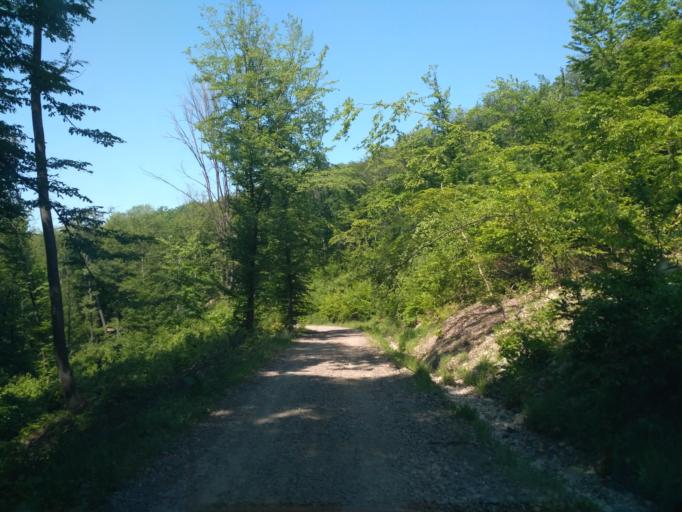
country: SK
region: Presovsky
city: Vranov nad Topl'ou
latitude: 48.8376
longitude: 21.4638
